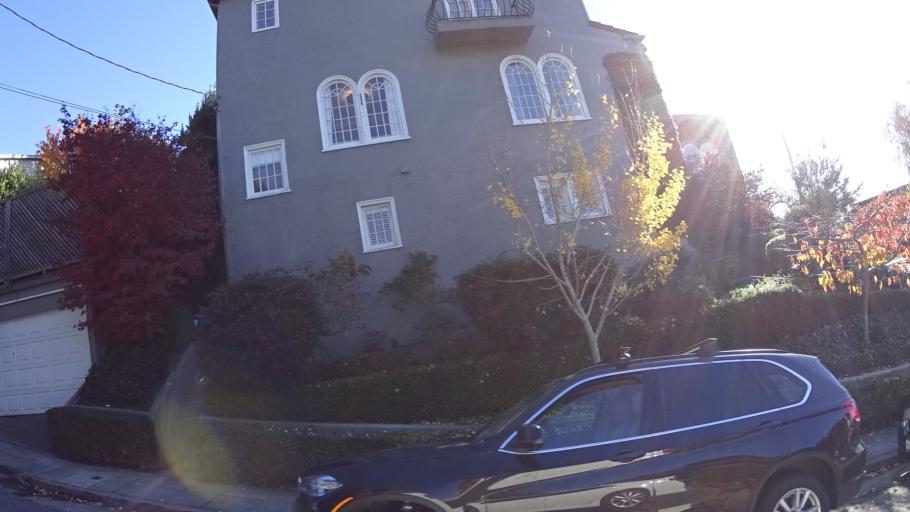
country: US
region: California
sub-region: Alameda County
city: Piedmont
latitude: 37.8256
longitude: -122.2278
